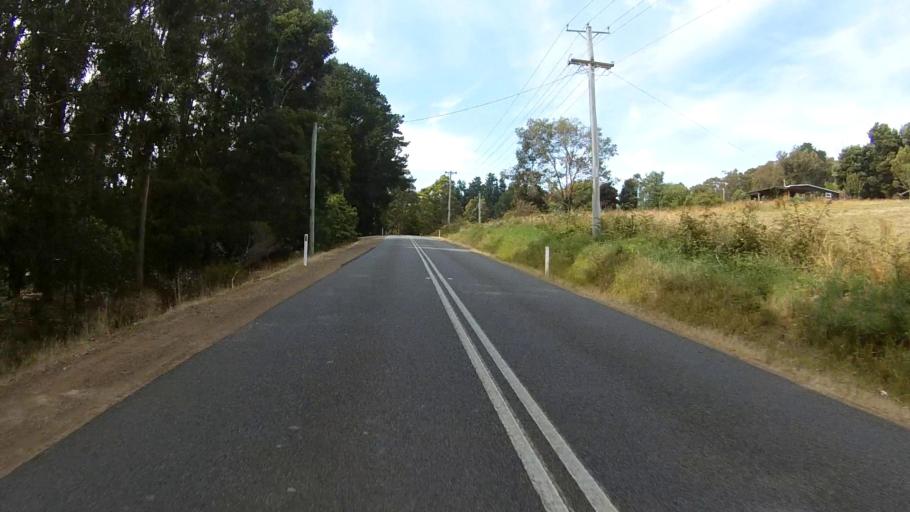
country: AU
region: Tasmania
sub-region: Kingborough
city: Kettering
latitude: -43.1838
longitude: 147.2410
